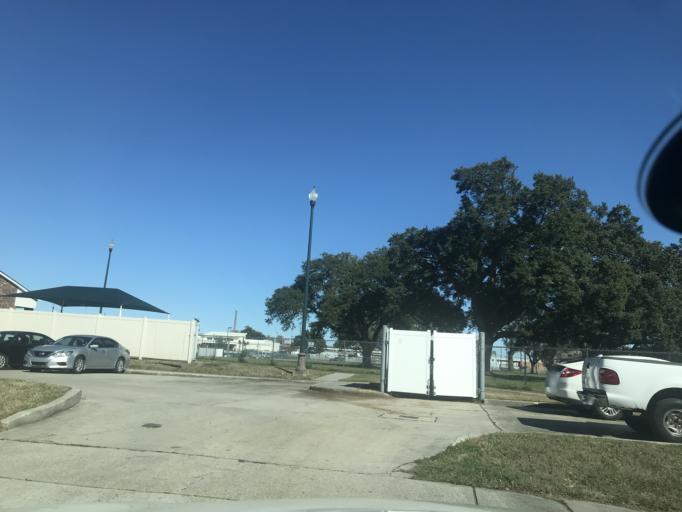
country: US
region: Louisiana
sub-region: Orleans Parish
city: New Orleans
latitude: 29.9510
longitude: -90.0930
